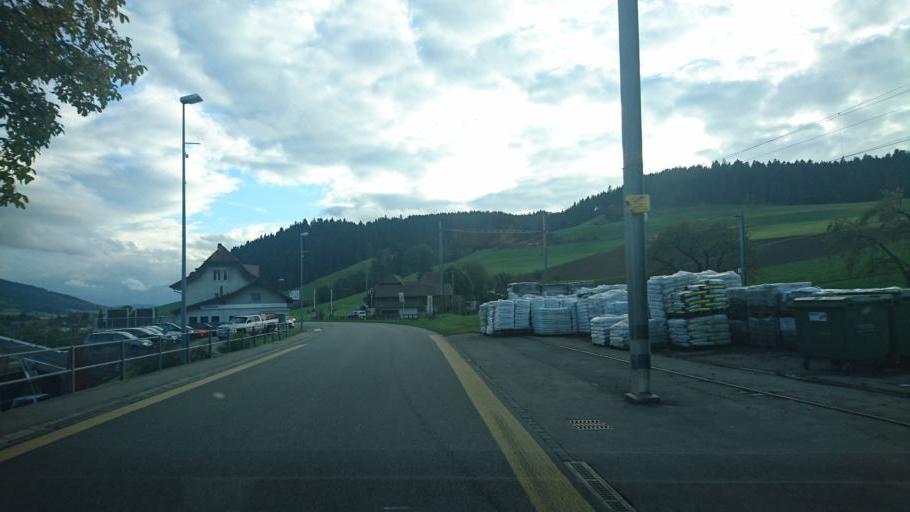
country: CH
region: Bern
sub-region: Bern-Mittelland District
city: Biglen
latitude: 46.9033
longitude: 7.6339
